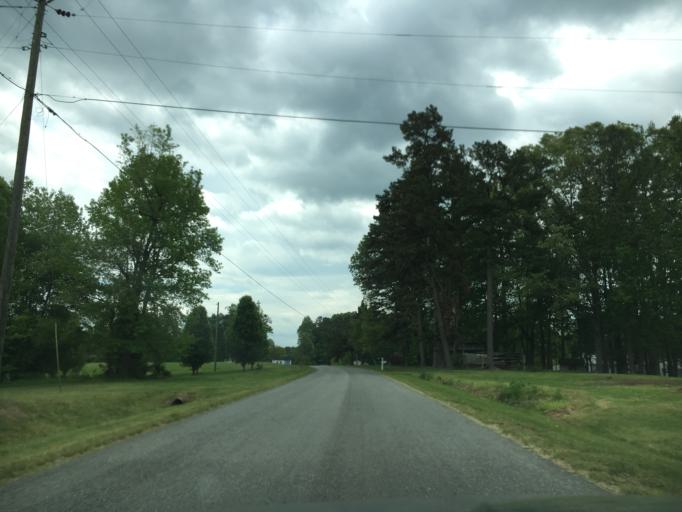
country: US
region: Virginia
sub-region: Halifax County
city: Halifax
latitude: 36.7997
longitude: -78.9426
